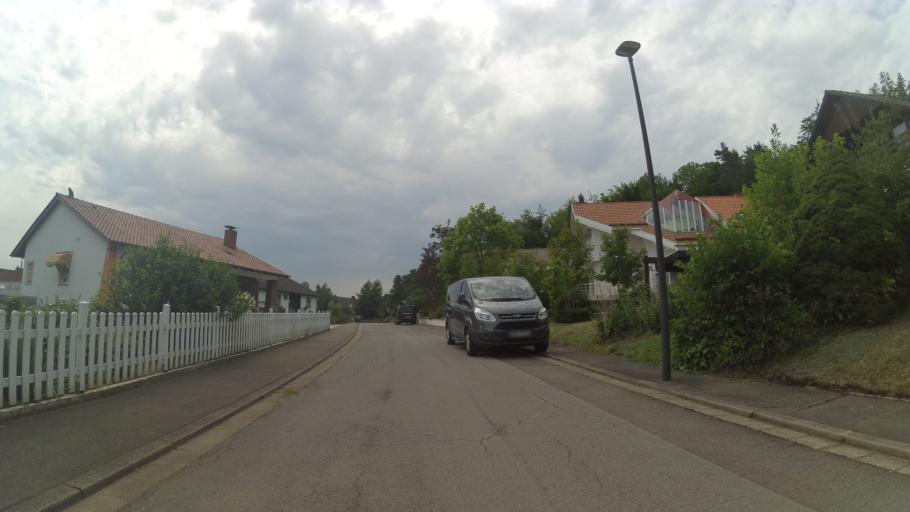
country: DE
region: Rheinland-Pfalz
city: Waldmohr
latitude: 49.3755
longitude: 7.3294
